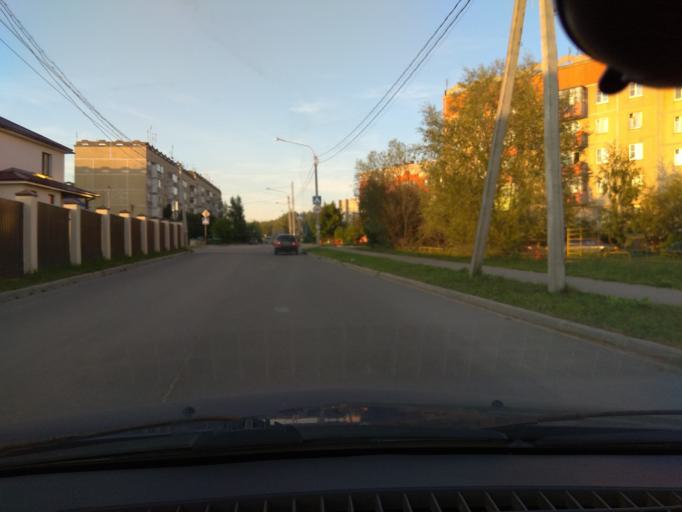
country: RU
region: Kaluga
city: Mstikhino
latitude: 54.5613
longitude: 36.1330
